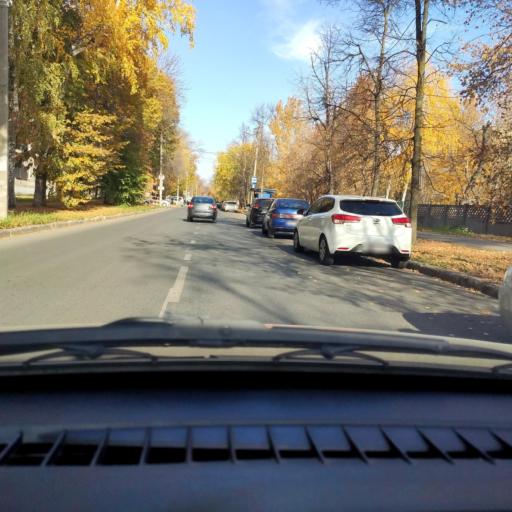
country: RU
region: Samara
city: Tol'yatti
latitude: 53.5003
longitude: 49.4094
